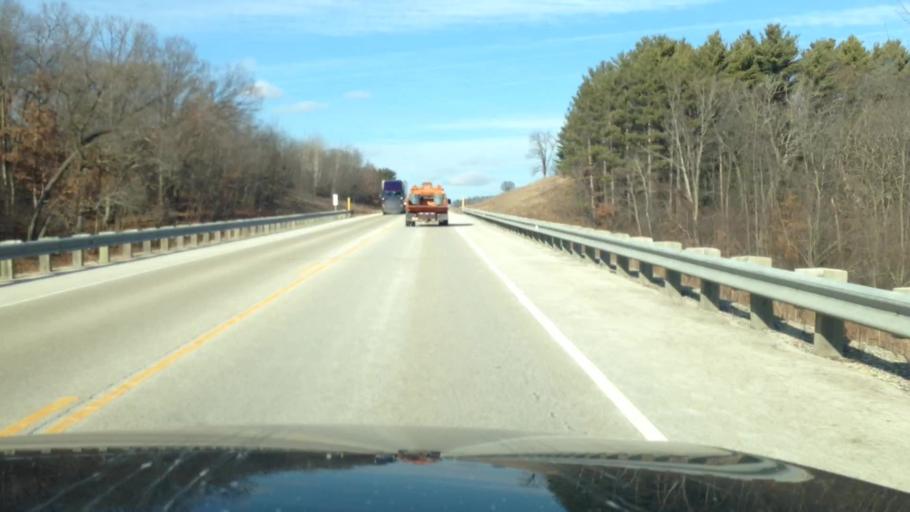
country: US
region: Wisconsin
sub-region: Walworth County
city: East Troy
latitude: 42.7366
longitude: -88.4059
